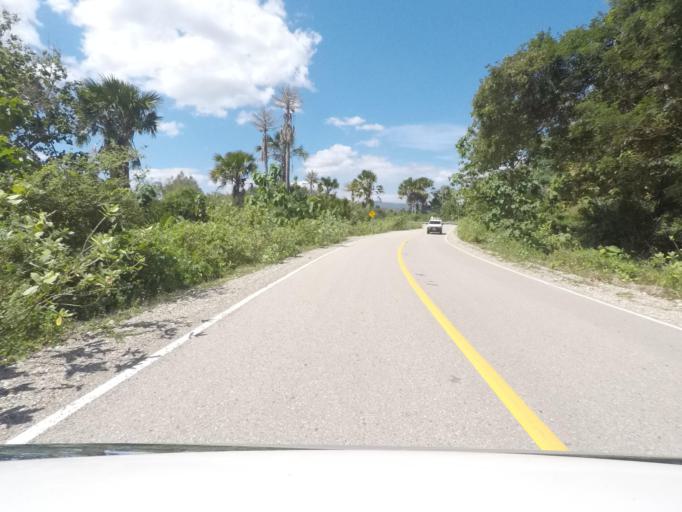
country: TL
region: Lautem
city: Lospalos
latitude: -8.4136
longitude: 126.8074
